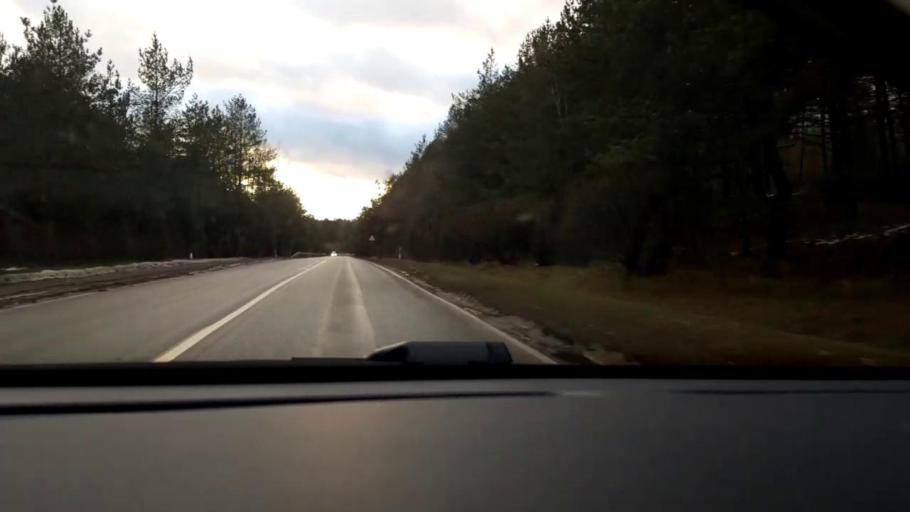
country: LT
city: Nemencine
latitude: 54.7913
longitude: 25.3880
